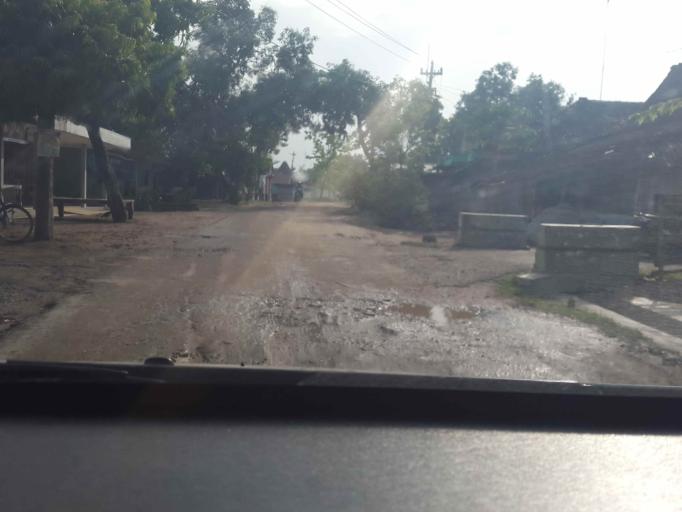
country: ID
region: Central Java
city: Grawan
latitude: -6.7674
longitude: 111.2909
